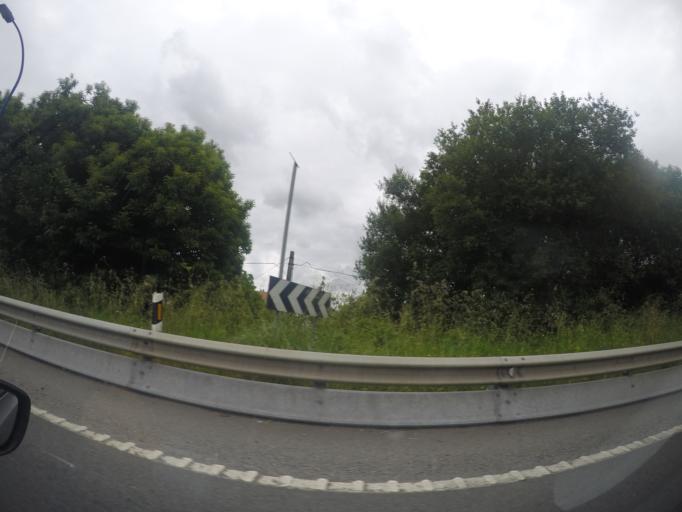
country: ES
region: Galicia
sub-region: Provincia da Coruna
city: Culleredo
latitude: 43.3063
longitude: -8.3808
